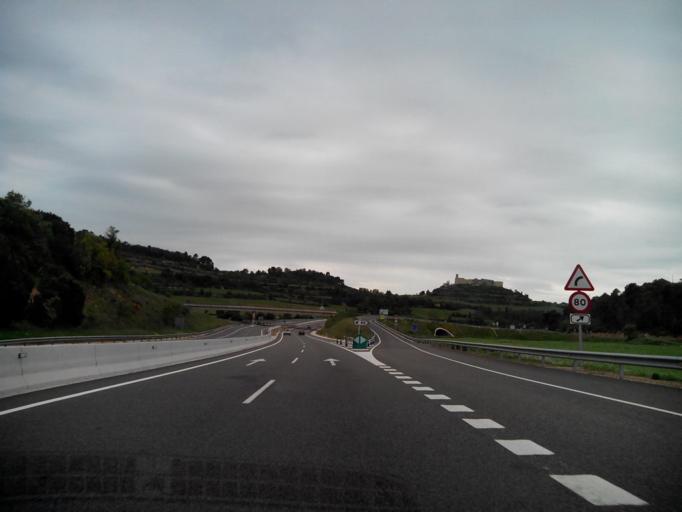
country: ES
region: Catalonia
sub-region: Provincia de Barcelona
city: Pujalt
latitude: 41.6987
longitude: 1.3479
